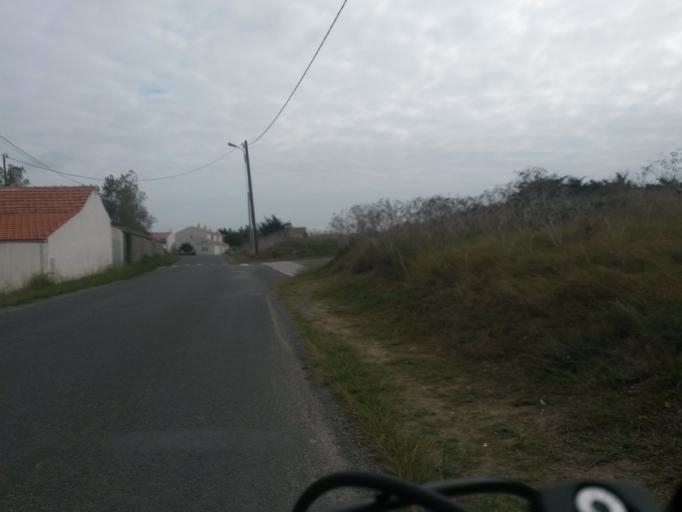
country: FR
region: Poitou-Charentes
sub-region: Departement de la Charente-Maritime
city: Saint-Denis-d'Oleron
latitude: 46.0131
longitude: -1.3917
